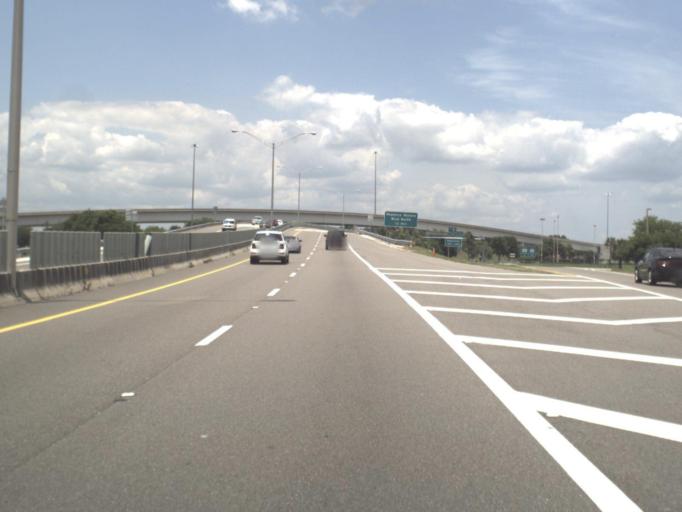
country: US
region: Florida
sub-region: Duval County
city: Jacksonville
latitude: 30.3203
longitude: -81.5588
